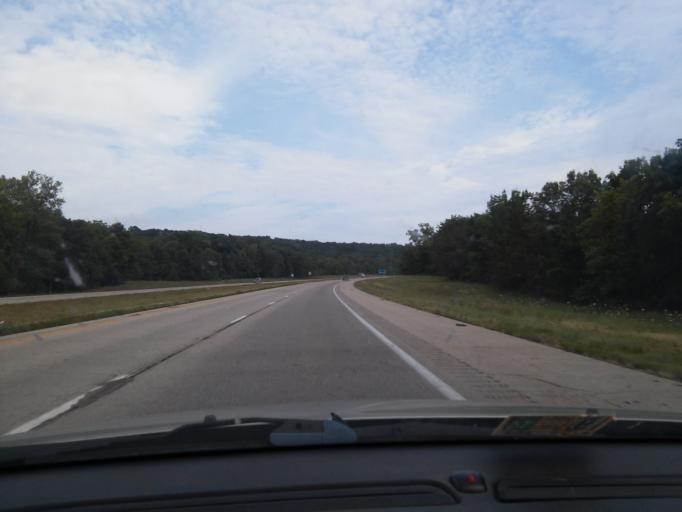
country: US
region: Ohio
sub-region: Ross County
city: North Fork Village
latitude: 39.3838
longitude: -83.0695
